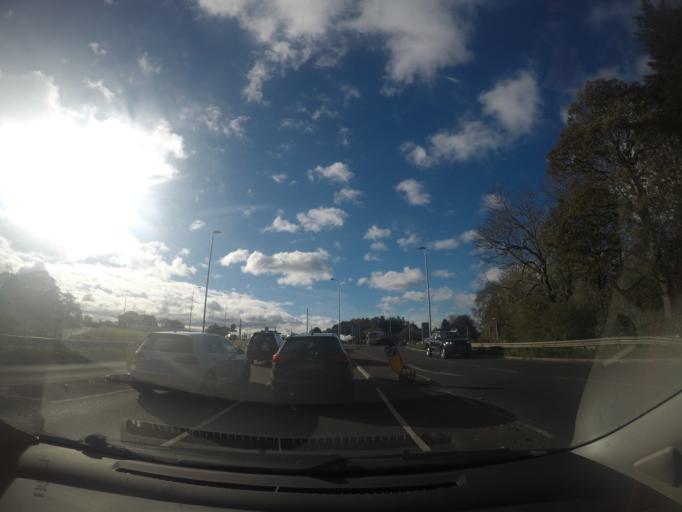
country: GB
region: England
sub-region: City of York
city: Nether Poppleton
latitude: 53.9733
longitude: -1.1427
